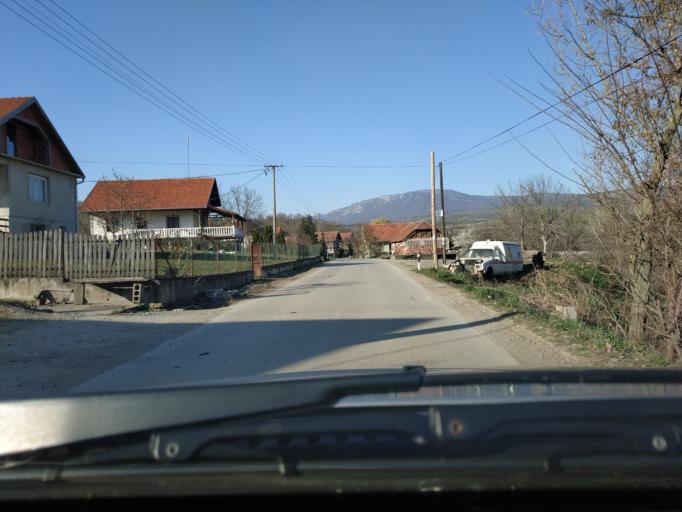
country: RS
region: Central Serbia
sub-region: Nisavski Okrug
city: Aleksinac
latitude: 43.5200
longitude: 21.7998
